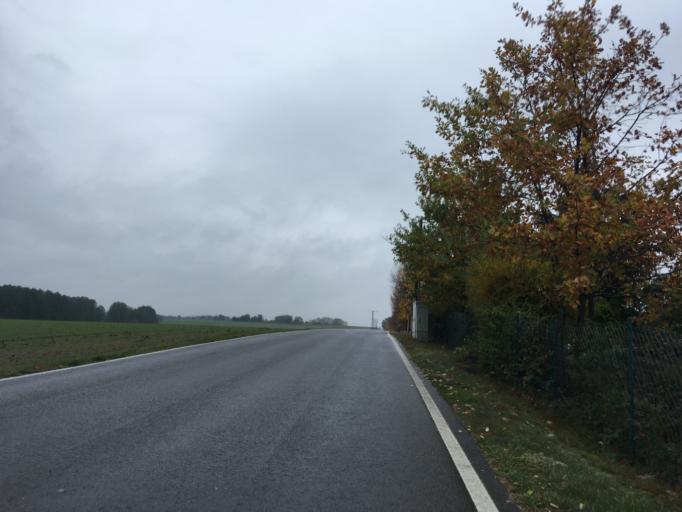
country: DE
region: Brandenburg
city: Friedland
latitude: 52.0596
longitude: 14.1896
